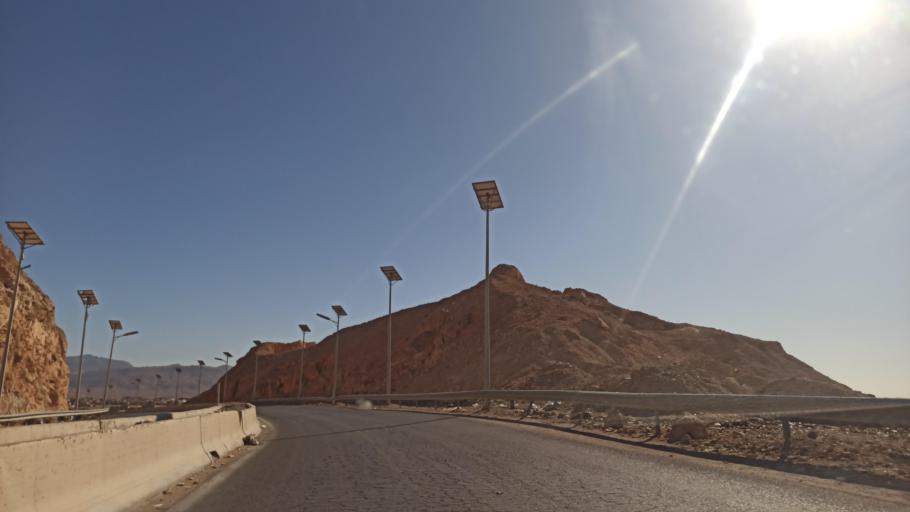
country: TN
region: Gafsa
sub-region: Gafsa Municipality
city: Gafsa
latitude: 34.4341
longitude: 8.7957
